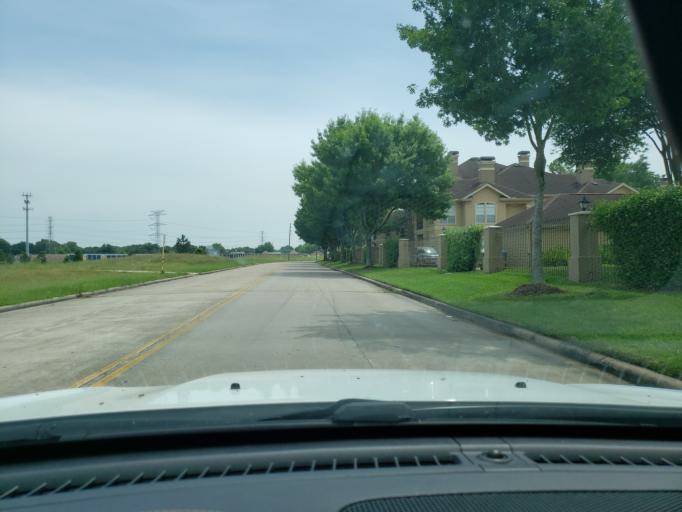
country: US
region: Texas
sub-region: Harris County
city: Jersey Village
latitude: 29.9131
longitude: -95.5810
